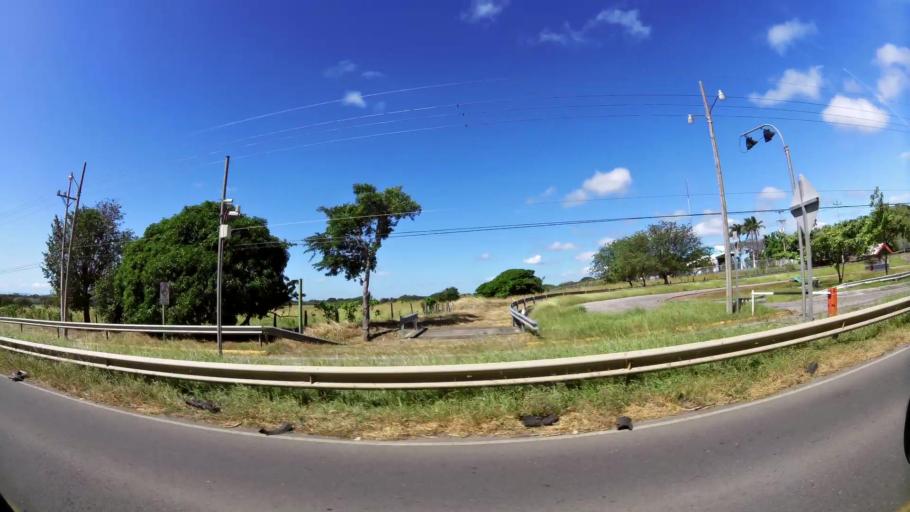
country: CR
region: Guanacaste
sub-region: Canton de Canas
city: Canas
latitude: 10.3893
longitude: -85.0815
